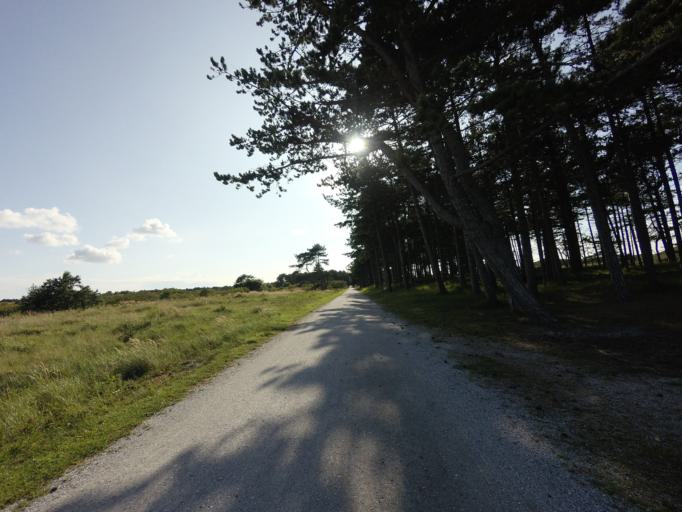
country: NL
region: Friesland
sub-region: Gemeente Terschelling
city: West-Terschelling
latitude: 53.3922
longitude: 5.2380
